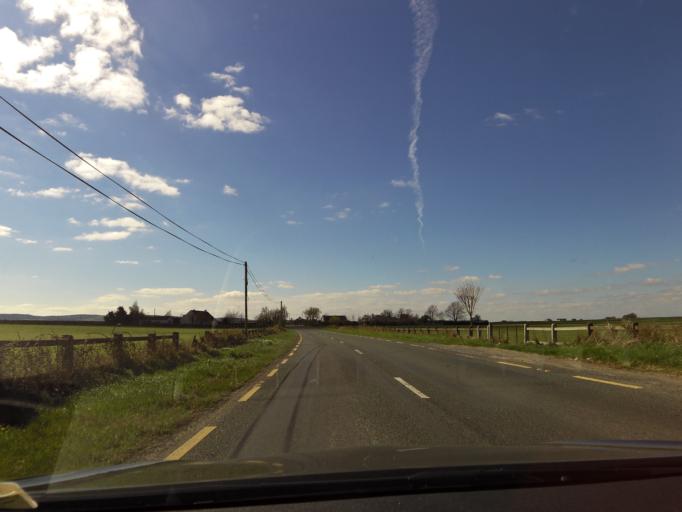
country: IE
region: Leinster
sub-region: Kildare
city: Athy
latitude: 53.0000
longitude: -7.0118
